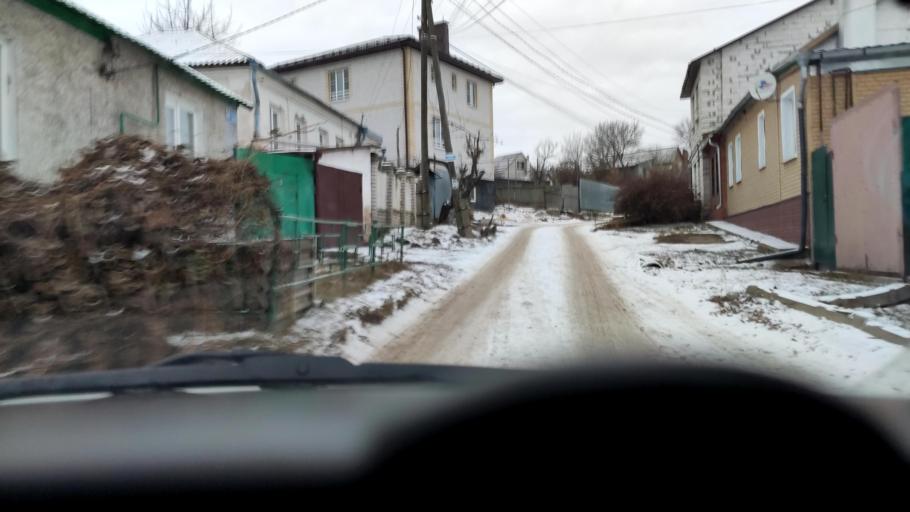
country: RU
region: Voronezj
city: Voronezh
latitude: 51.6326
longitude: 39.2051
